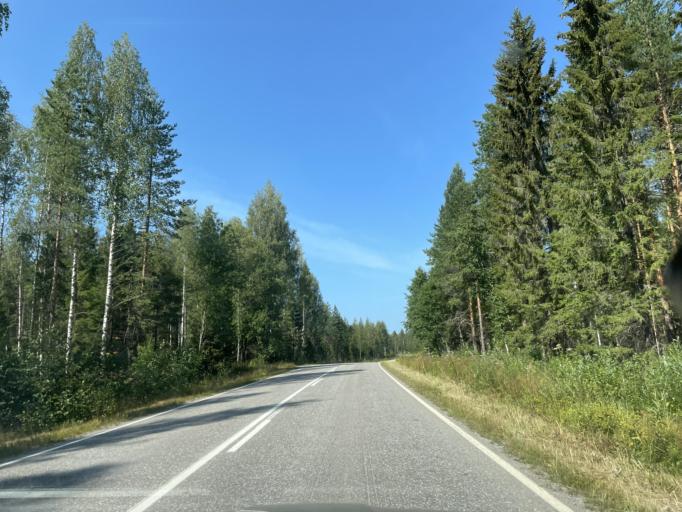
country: FI
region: Central Finland
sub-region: Saarijaervi-Viitasaari
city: Pihtipudas
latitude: 63.3658
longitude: 25.6955
